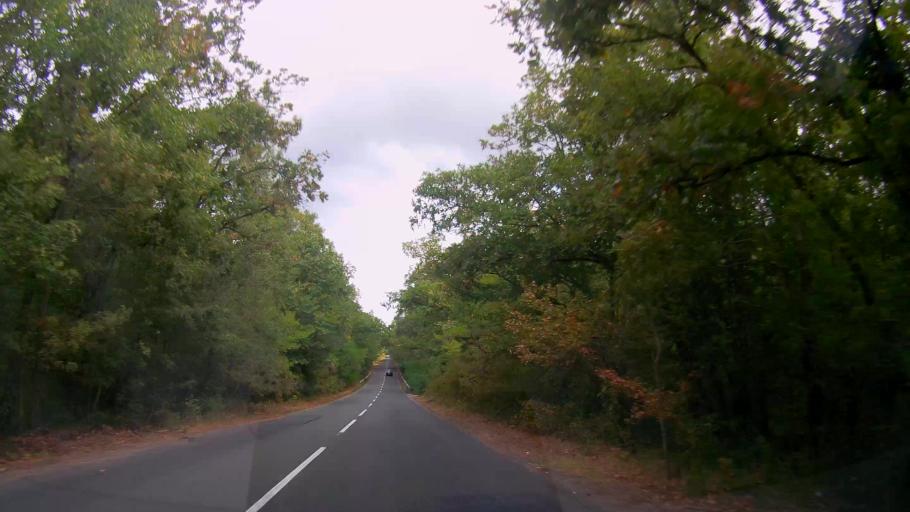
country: BG
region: Burgas
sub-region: Obshtina Primorsko
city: Primorsko
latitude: 42.2854
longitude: 27.7366
